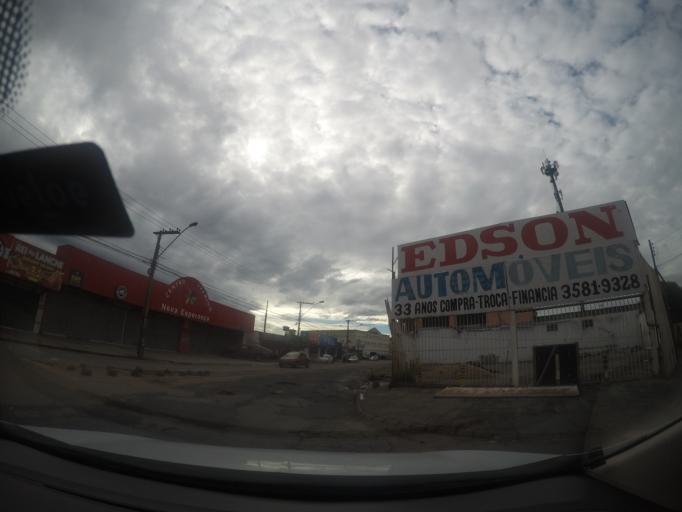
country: BR
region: Goias
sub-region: Goiania
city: Goiania
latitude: -16.6465
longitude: -49.3234
